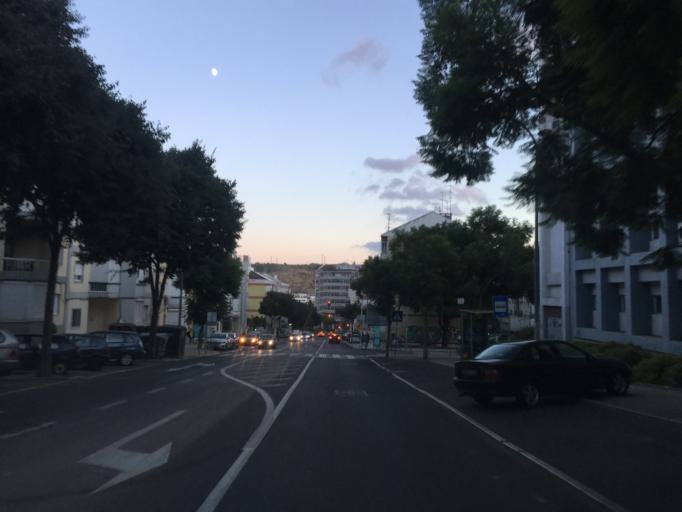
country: PT
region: Lisbon
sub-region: Odivelas
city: Odivelas
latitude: 38.7929
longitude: -9.1775
